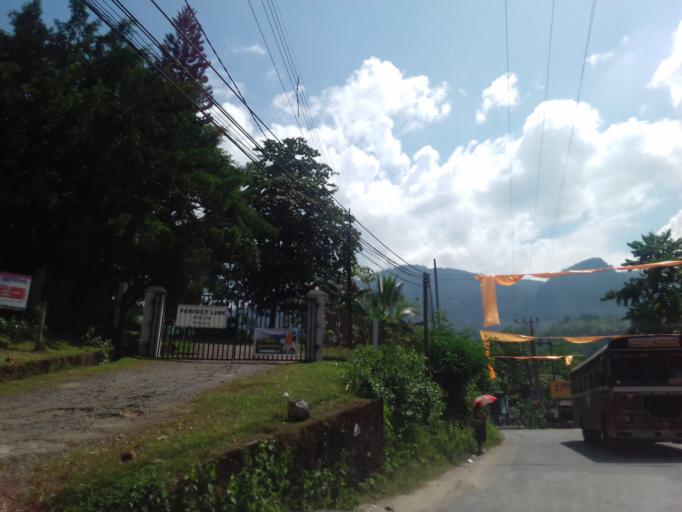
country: LK
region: Central
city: Hatton
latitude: 6.9975
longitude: 80.3594
